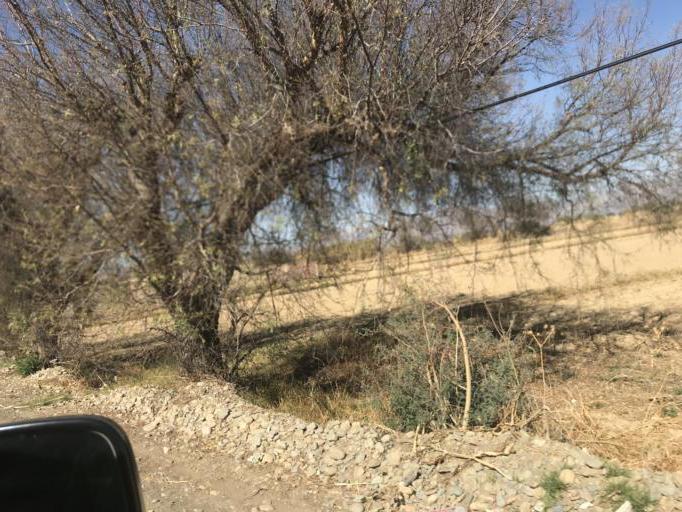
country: BO
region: Cochabamba
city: Punata
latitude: -17.5634
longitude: -65.8816
